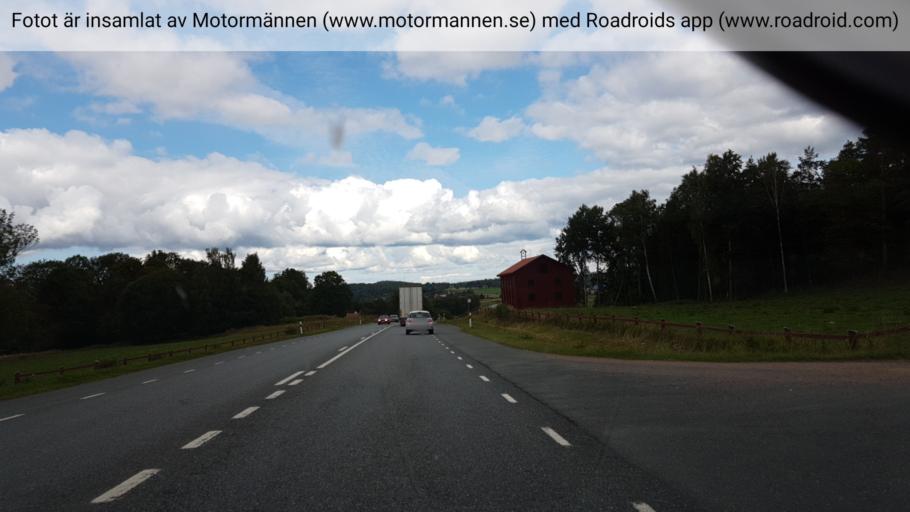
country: SE
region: Joenkoeping
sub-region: Tranas Kommun
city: Tranas
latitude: 57.9757
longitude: 14.9141
